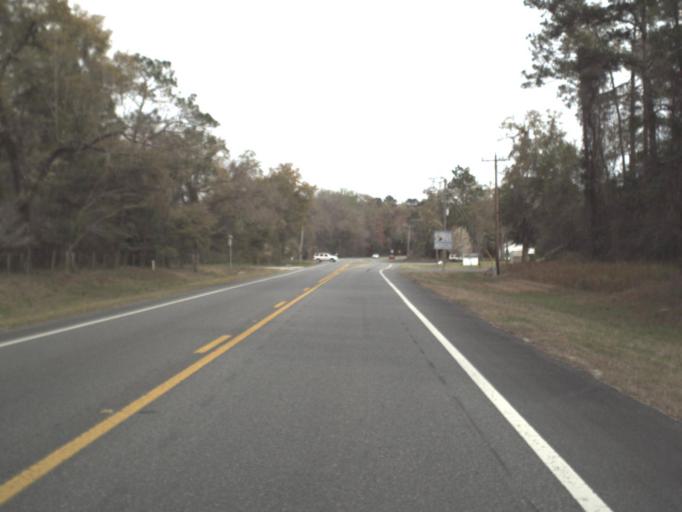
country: US
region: Florida
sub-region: Wakulla County
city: Crawfordville
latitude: 30.2530
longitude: -84.3259
